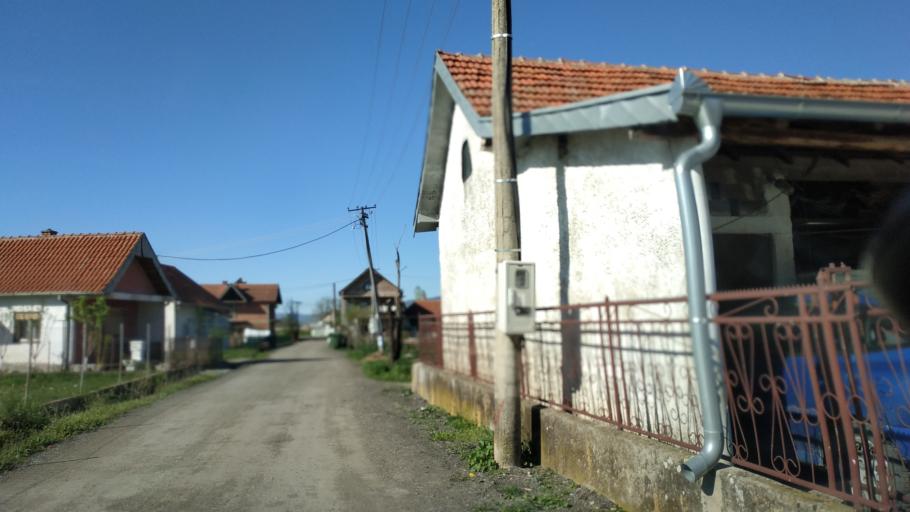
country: RS
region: Central Serbia
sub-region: Nisavski Okrug
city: Aleksinac
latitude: 43.5110
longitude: 21.6873
